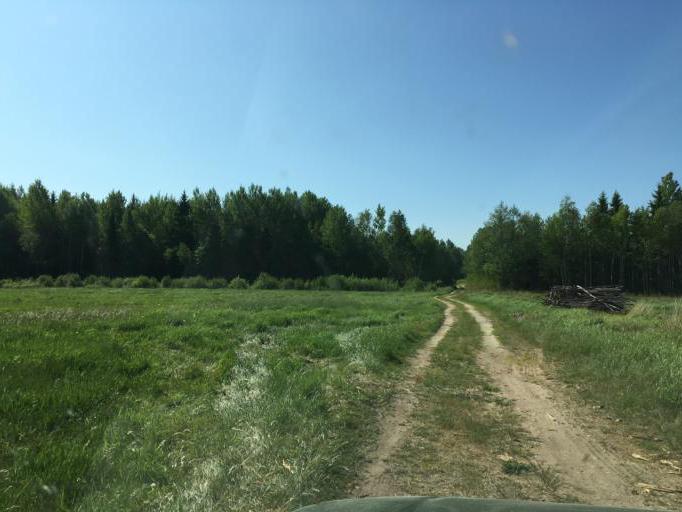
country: LV
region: Ventspils
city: Ventspils
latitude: 57.4804
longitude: 21.7630
